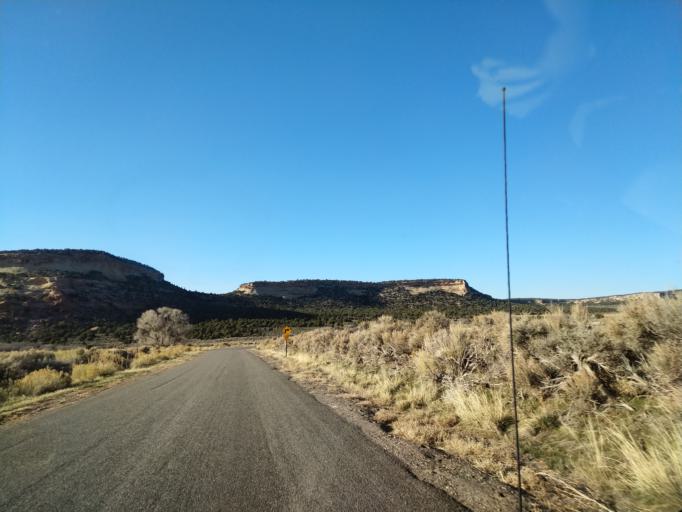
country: US
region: Colorado
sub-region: Mesa County
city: Loma
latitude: 38.9521
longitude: -109.0313
